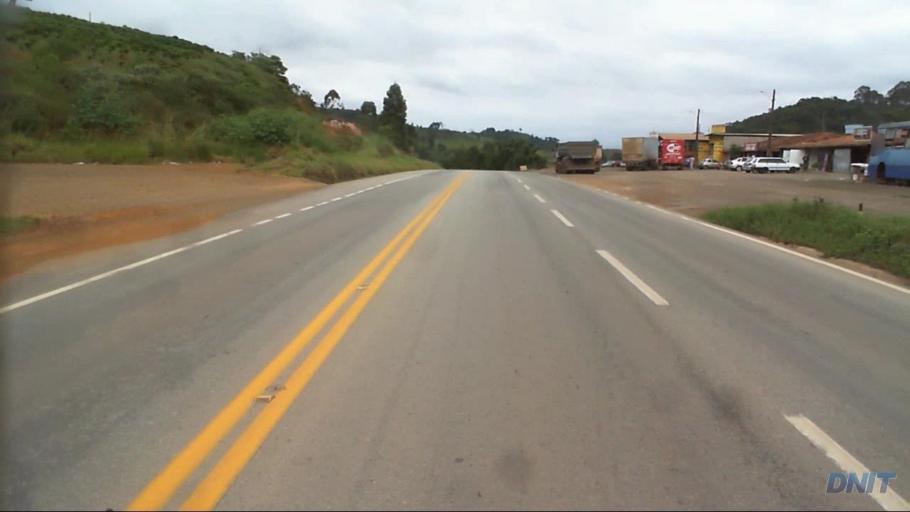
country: BR
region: Minas Gerais
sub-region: Joao Monlevade
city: Joao Monlevade
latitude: -19.8430
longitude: -43.2019
